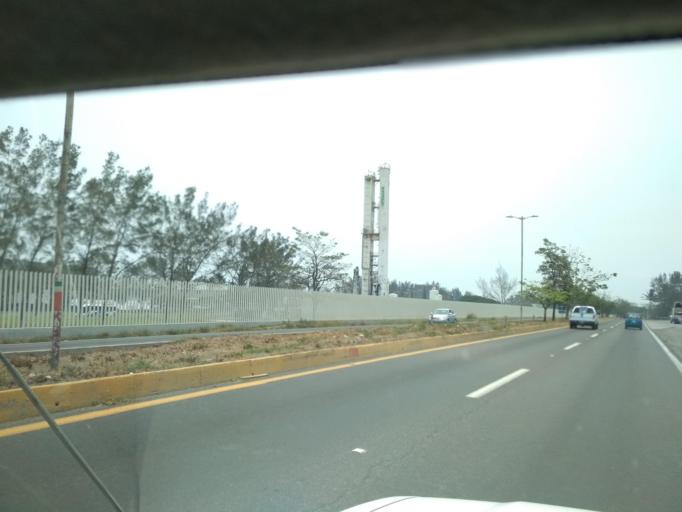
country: MX
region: Veracruz
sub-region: Veracruz
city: Oasis
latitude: 19.1746
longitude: -96.2372
